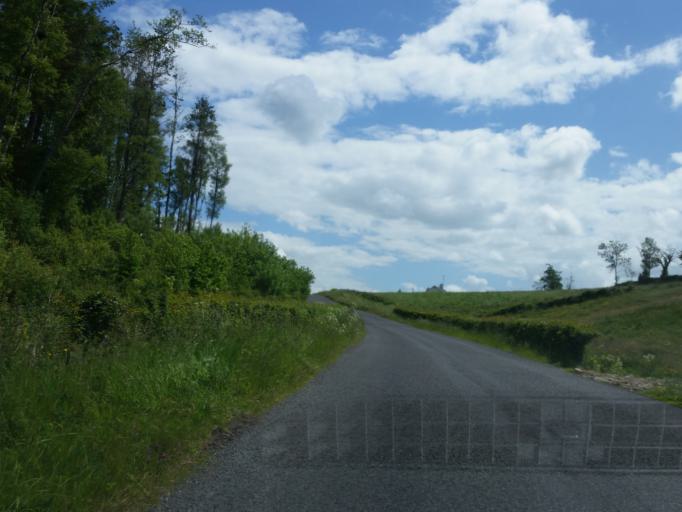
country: GB
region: Northern Ireland
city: Fivemiletown
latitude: 54.3538
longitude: -7.3010
